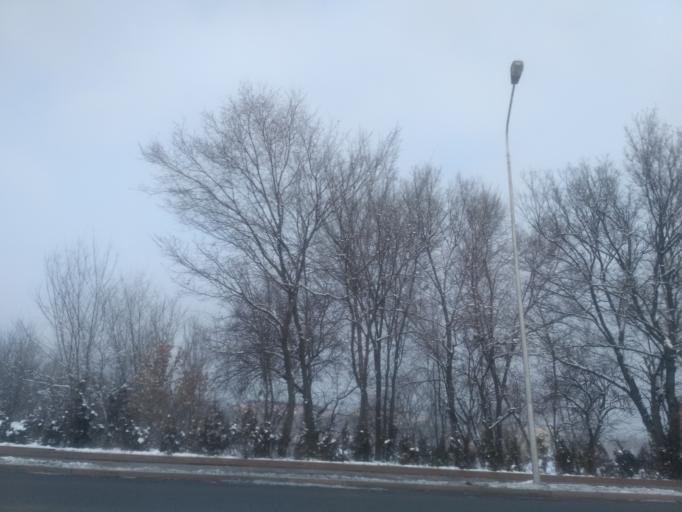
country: KZ
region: Almaty Qalasy
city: Almaty
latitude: 43.2171
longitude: 76.9272
